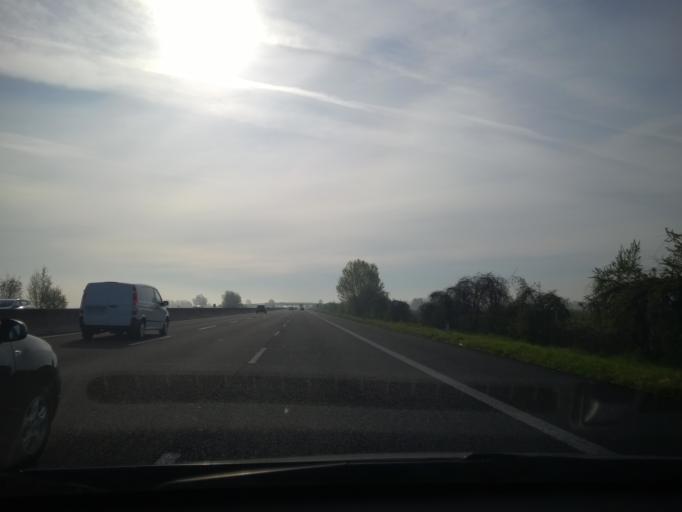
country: IT
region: Emilia-Romagna
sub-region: Provincia di Bologna
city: Castel Guelfo di Bologna
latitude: 44.4048
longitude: 11.6790
